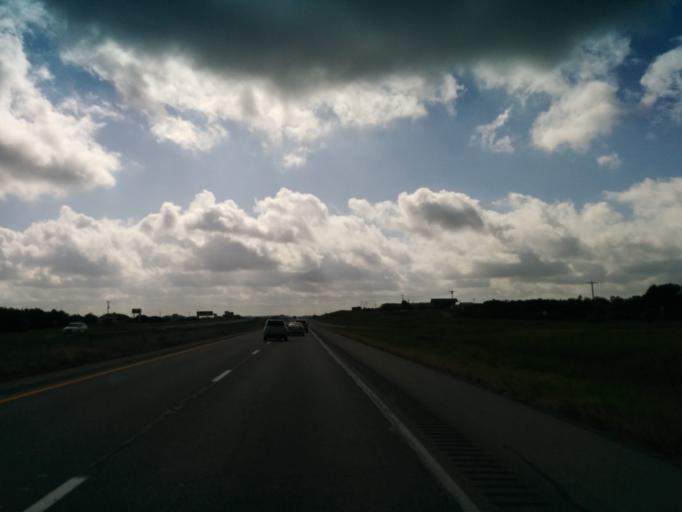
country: US
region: Texas
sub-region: Caldwell County
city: Luling
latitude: 29.6509
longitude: -97.6583
